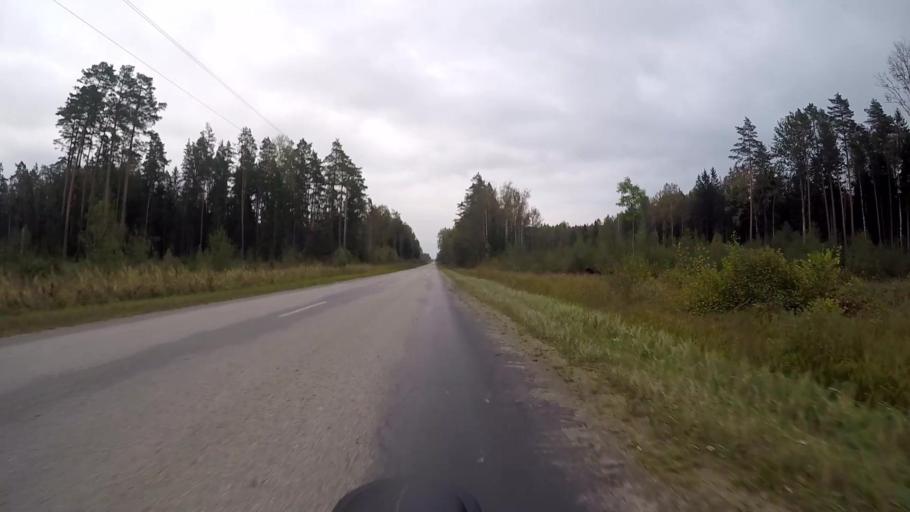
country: LV
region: Saulkrastu
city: Saulkrasti
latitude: 57.2718
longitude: 24.4893
